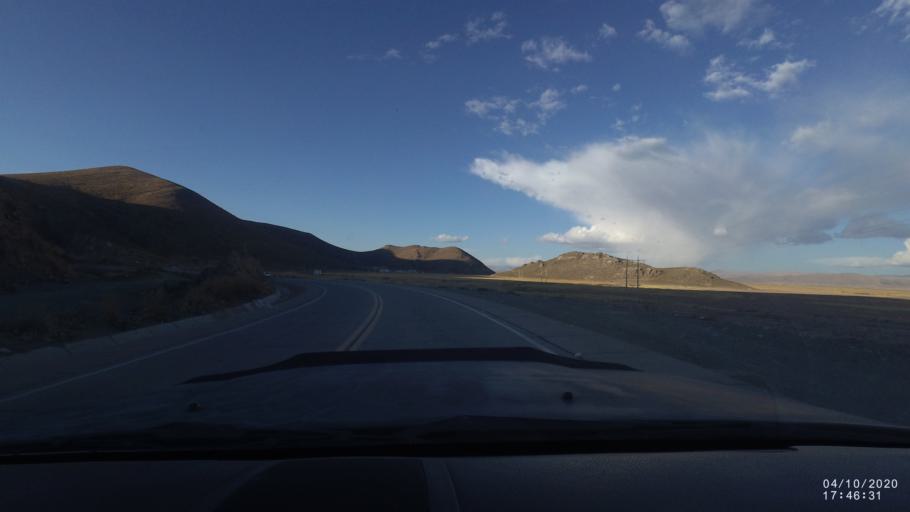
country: BO
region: Oruro
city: Oruro
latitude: -18.0312
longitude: -67.1475
